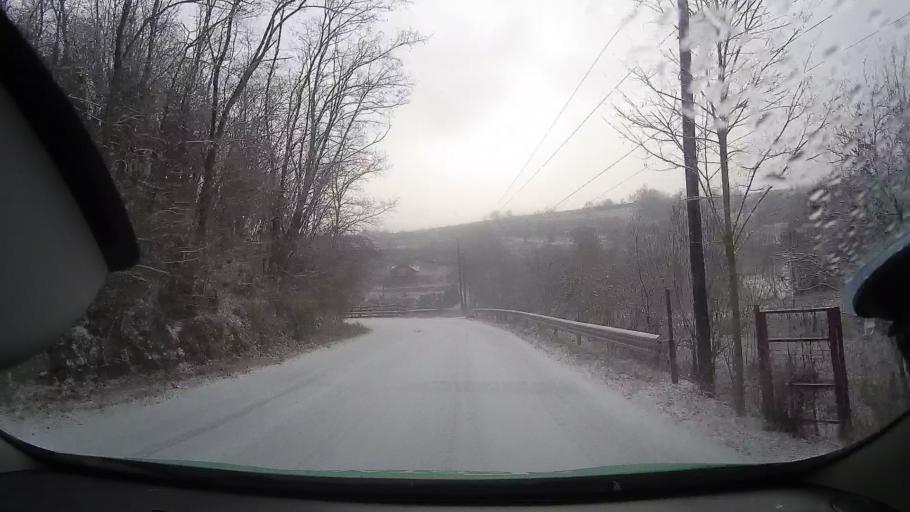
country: RO
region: Alba
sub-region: Comuna Livezile
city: Livezile
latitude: 46.3672
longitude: 23.5926
